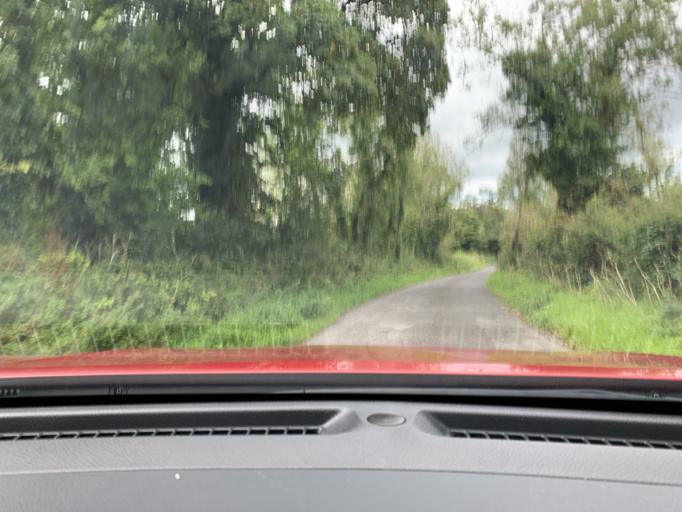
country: IE
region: Connaught
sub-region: Sligo
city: Collooney
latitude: 54.1632
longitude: -8.4287
